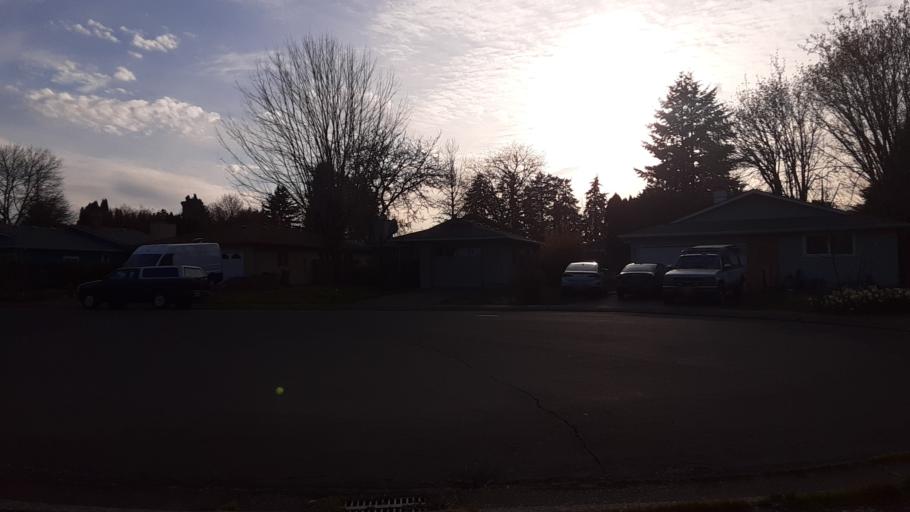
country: US
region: Oregon
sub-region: Benton County
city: Corvallis
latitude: 44.5471
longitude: -123.2581
